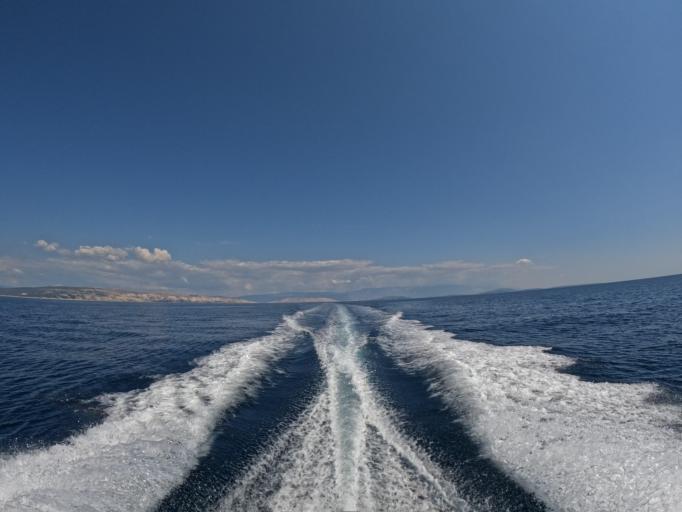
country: HR
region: Primorsko-Goranska
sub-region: Grad Krk
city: Krk
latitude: 44.9253
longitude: 14.5407
